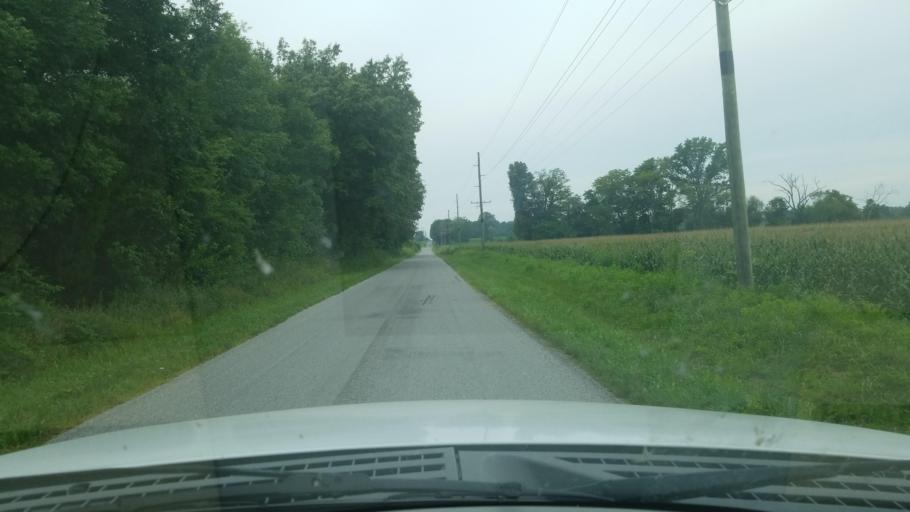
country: US
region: Illinois
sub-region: Saline County
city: Eldorado
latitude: 37.8630
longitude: -88.5245
